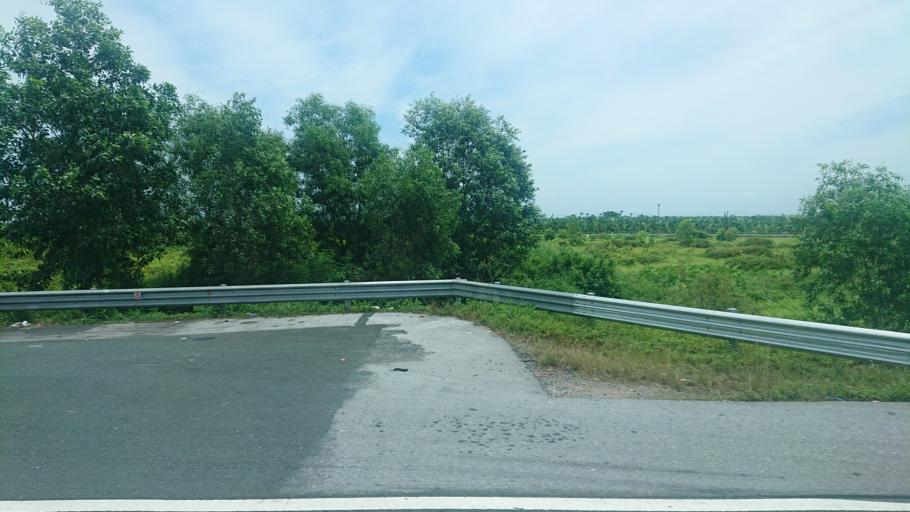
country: VN
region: Hai Phong
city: An Lao
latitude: 20.8148
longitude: 106.4944
